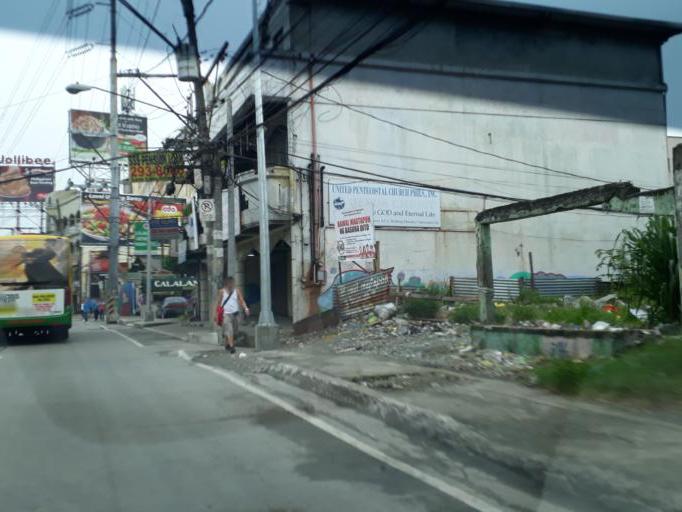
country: PH
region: Metro Manila
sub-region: Caloocan City
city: Niugan
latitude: 14.6720
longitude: 120.9821
